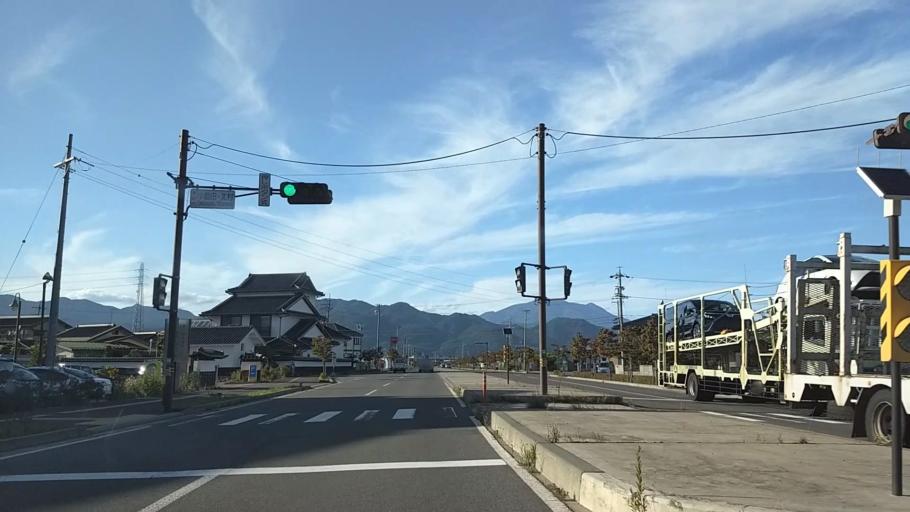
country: JP
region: Nagano
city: Nagano-shi
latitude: 36.5973
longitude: 138.1822
